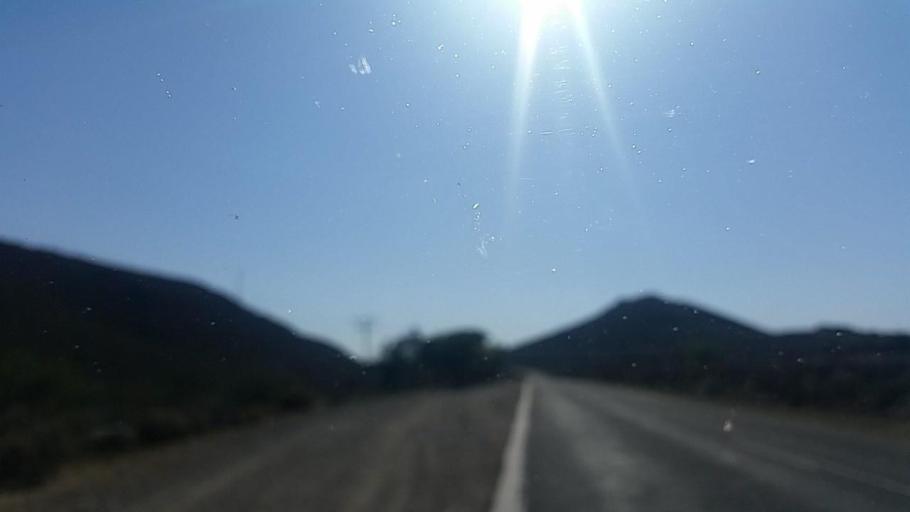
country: ZA
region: Eastern Cape
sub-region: Cacadu District Municipality
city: Willowmore
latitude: -33.3767
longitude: 23.4213
